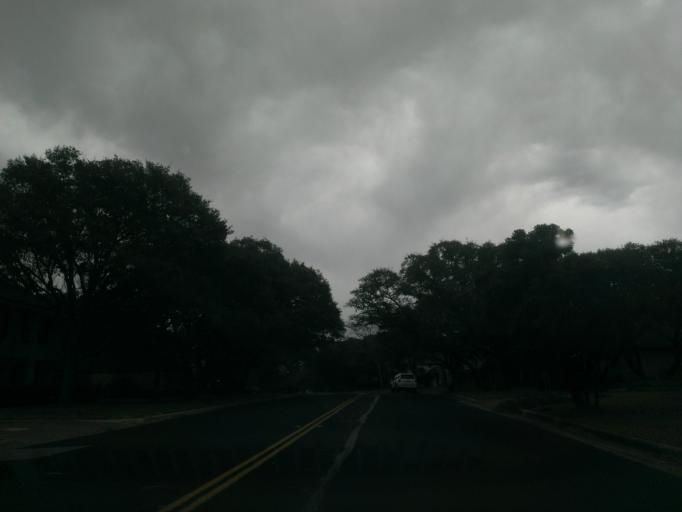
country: US
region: Texas
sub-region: Williamson County
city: Jollyville
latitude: 30.3671
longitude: -97.7682
